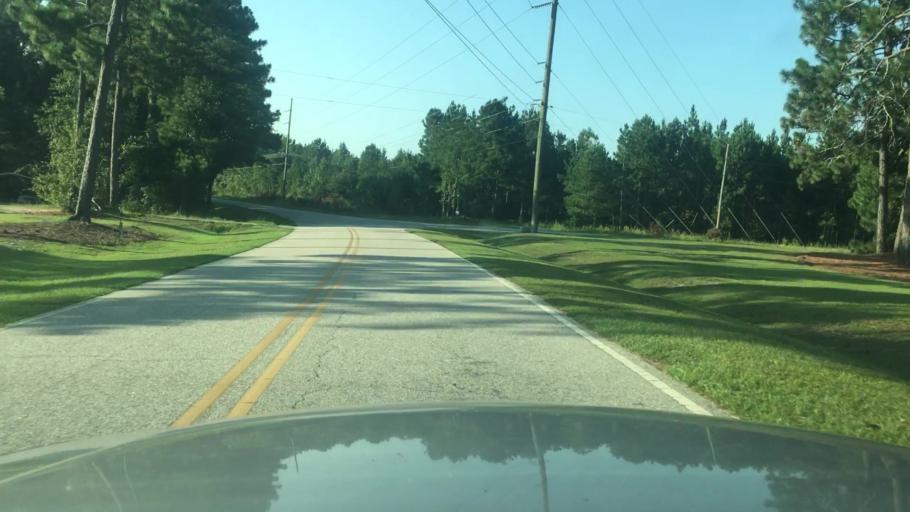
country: US
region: North Carolina
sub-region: Cumberland County
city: Spring Lake
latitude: 35.2114
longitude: -78.8956
